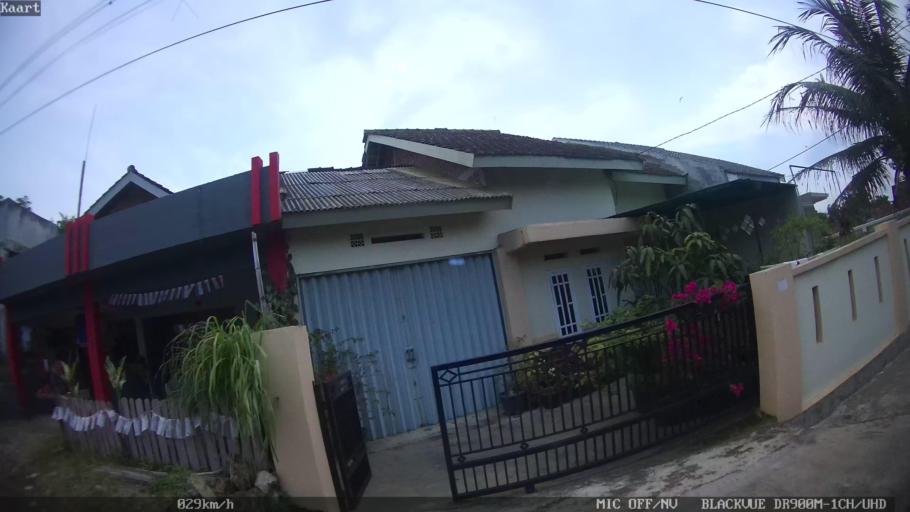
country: ID
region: Lampung
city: Bandarlampung
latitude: -5.4071
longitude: 105.2251
